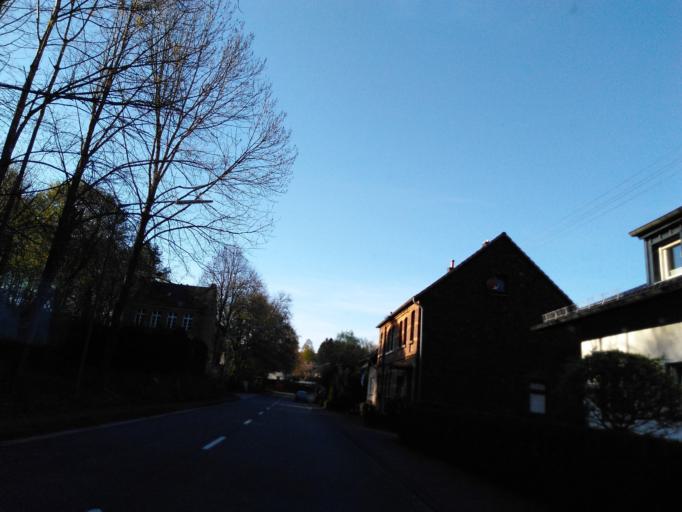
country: DE
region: North Rhine-Westphalia
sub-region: Regierungsbezirk Koln
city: Much
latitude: 50.9273
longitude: 7.4399
